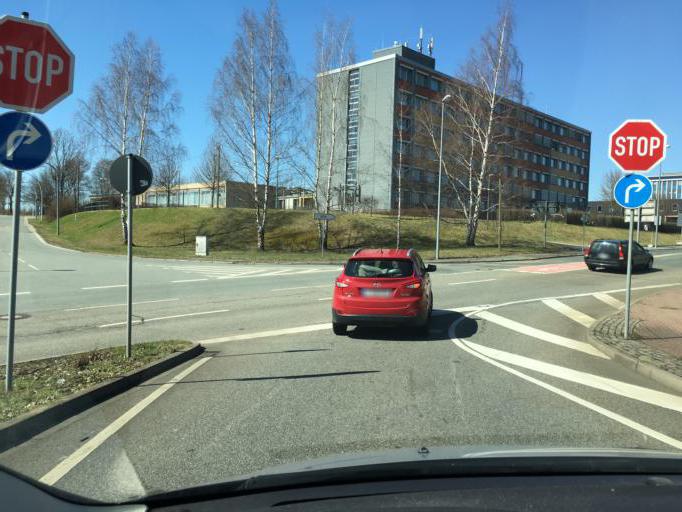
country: DE
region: Saxony
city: Neukirchen
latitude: 50.8050
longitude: 12.8436
